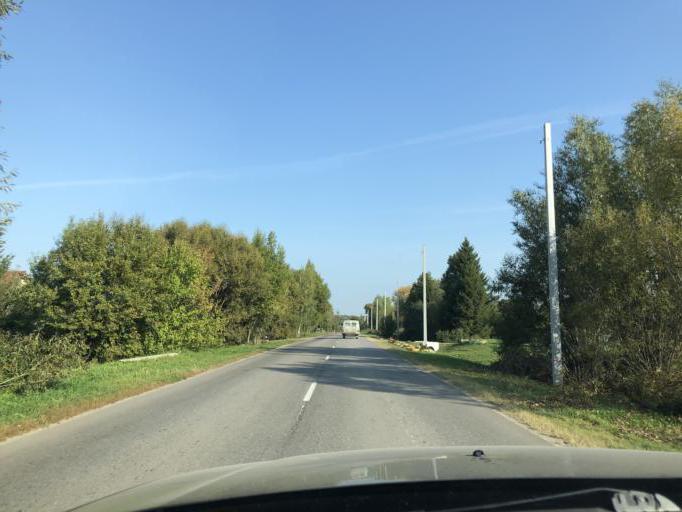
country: RU
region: Tula
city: Novogurovskiy
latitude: 54.4083
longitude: 37.3106
